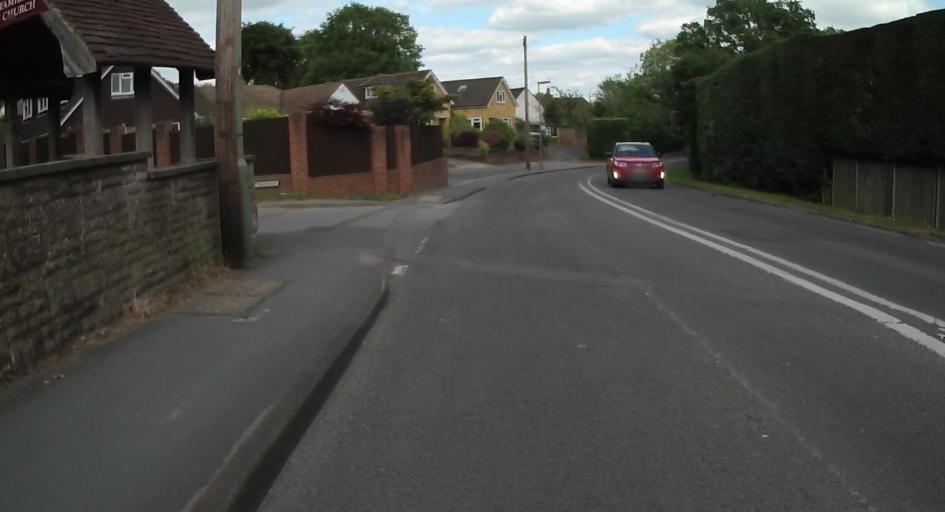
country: GB
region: England
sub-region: Surrey
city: Hale
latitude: 51.2380
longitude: -0.7914
